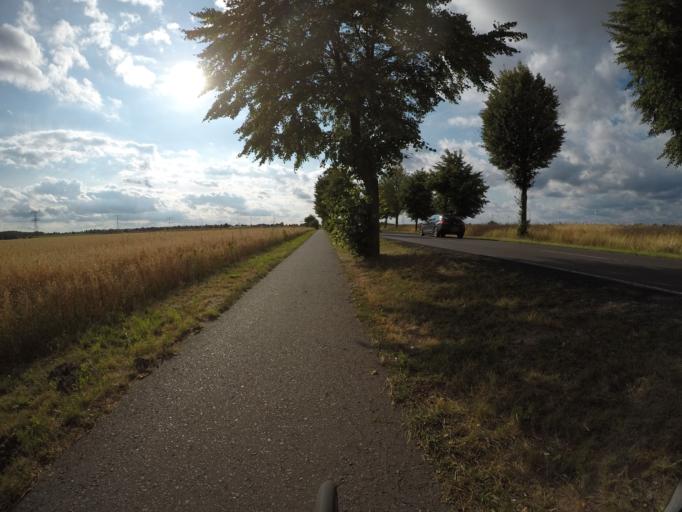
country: DE
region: Berlin
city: Falkenberg
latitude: 52.5892
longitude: 13.5552
